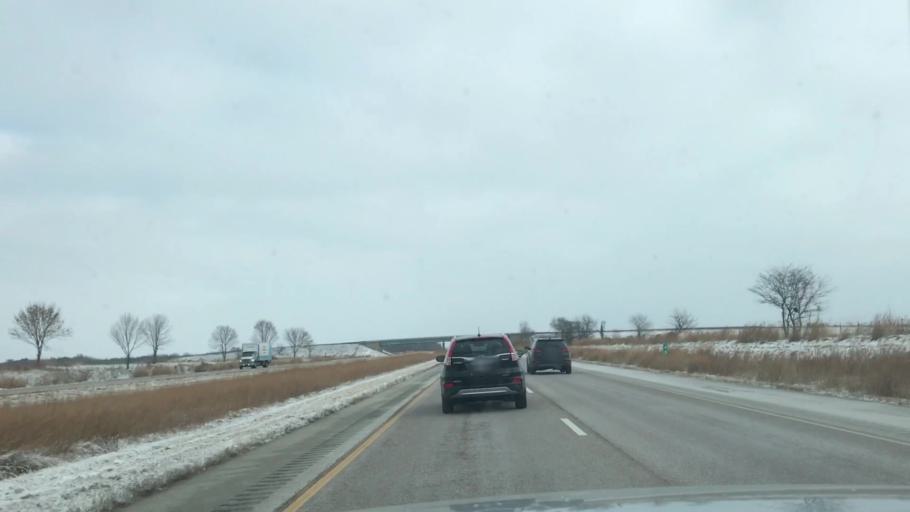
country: US
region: Illinois
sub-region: Macoupin County
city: Mount Olive
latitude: 39.1176
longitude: -89.7218
